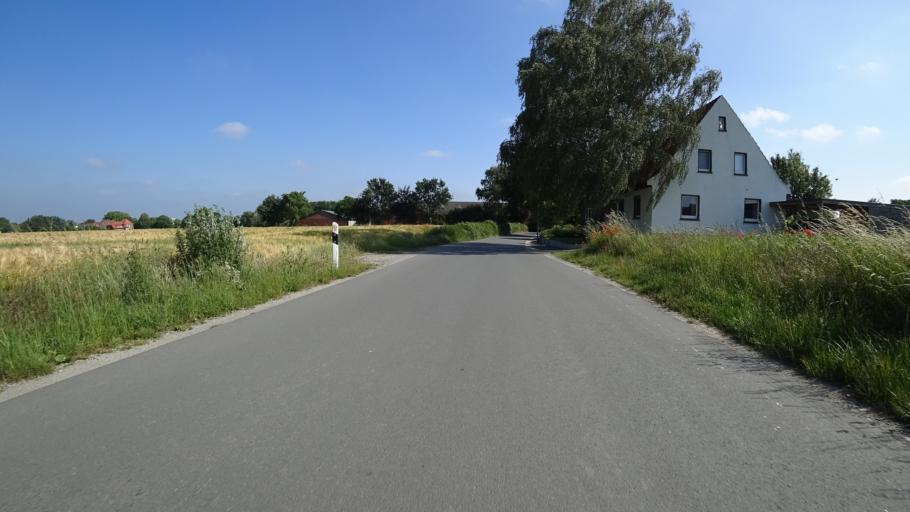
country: DE
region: North Rhine-Westphalia
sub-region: Regierungsbezirk Arnsberg
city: Lippstadt
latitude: 51.6650
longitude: 8.3809
